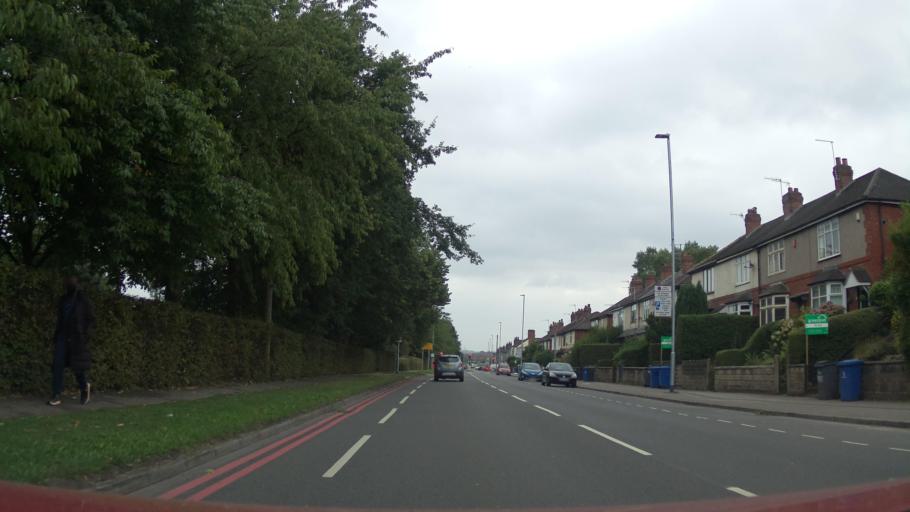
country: GB
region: England
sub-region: Stoke-on-Trent
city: Stoke-on-Trent
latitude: 53.0123
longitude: -2.1725
